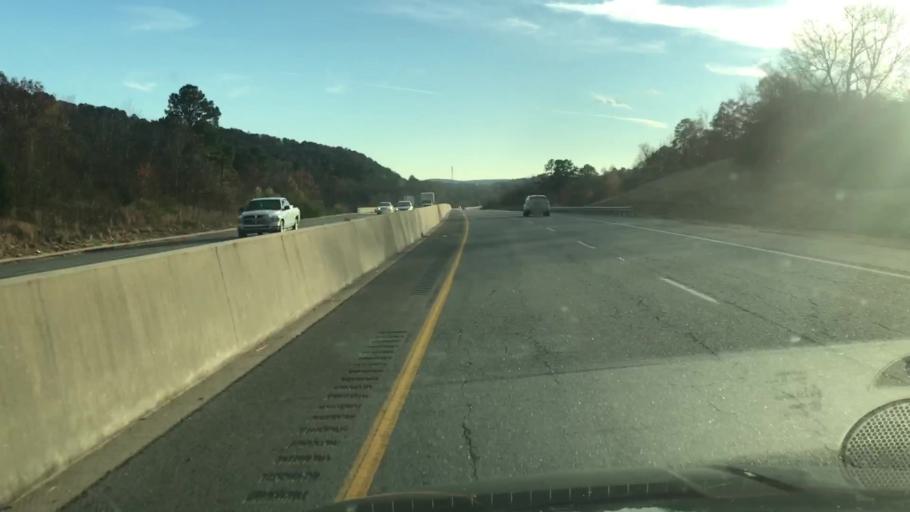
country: US
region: Arkansas
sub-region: Garland County
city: Hot Springs
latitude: 34.4873
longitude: -92.9805
